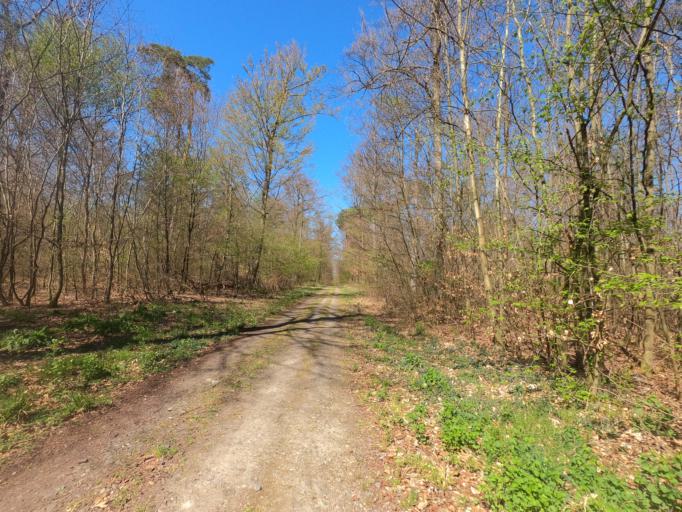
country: DE
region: Hesse
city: Morfelden-Walldorf
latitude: 49.9550
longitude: 8.5719
